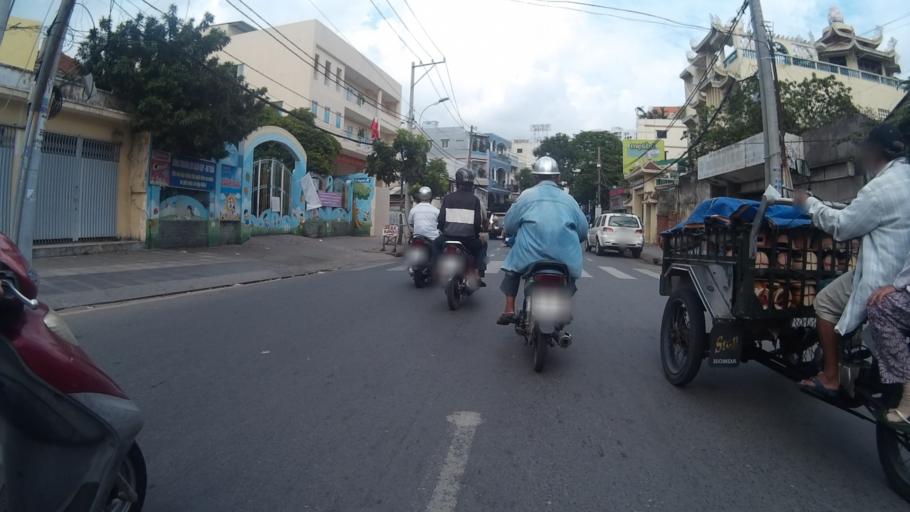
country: VN
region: Ho Chi Minh City
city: Quan Phu Nhuan
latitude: 10.7891
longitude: 106.6856
